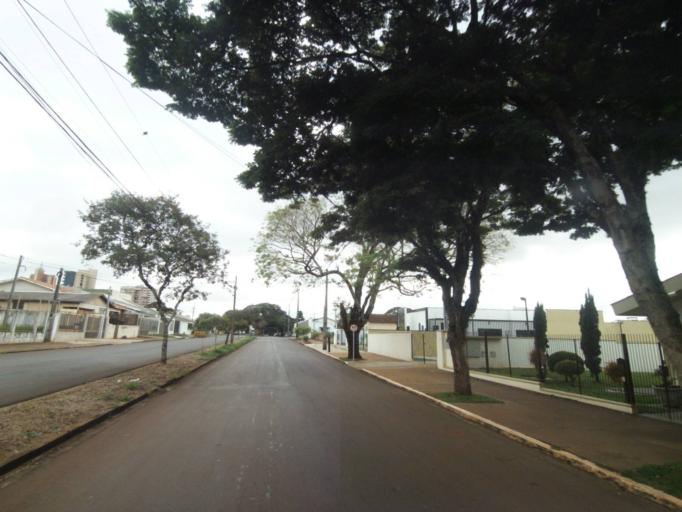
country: BR
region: Parana
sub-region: Campo Mourao
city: Campo Mourao
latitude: -24.0480
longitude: -52.3754
